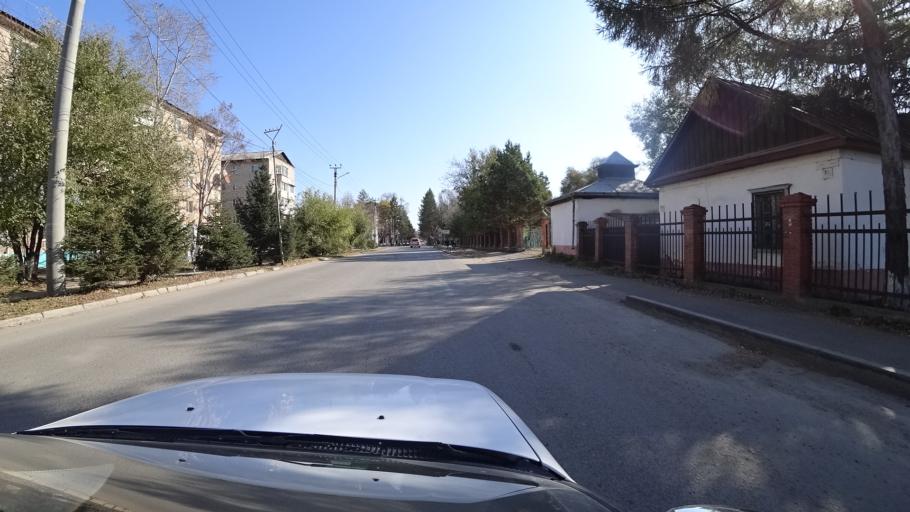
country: RU
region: Primorskiy
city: Dal'nerechensk
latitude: 45.9328
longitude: 133.7297
